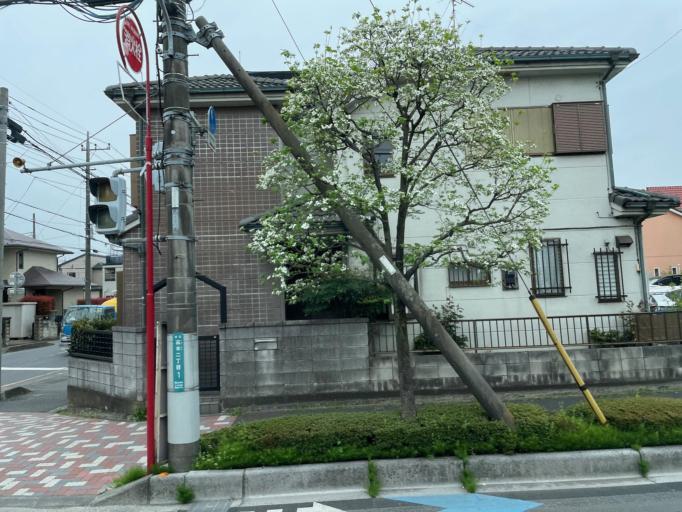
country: JP
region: Saitama
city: Saitama
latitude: 35.8871
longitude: 139.6904
